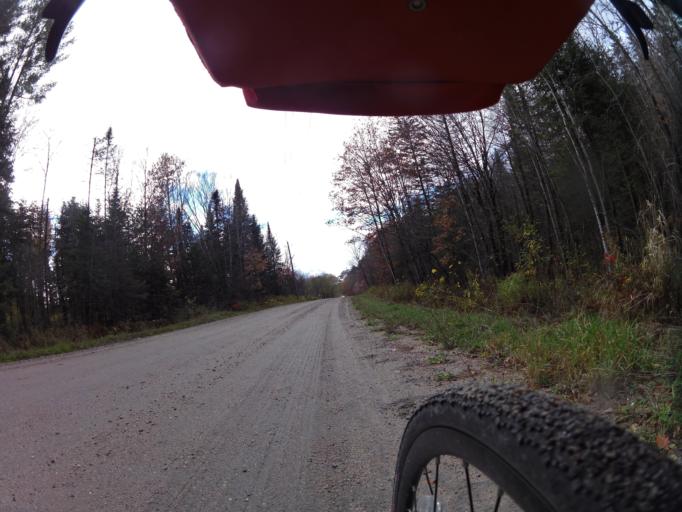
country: CA
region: Quebec
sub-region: Outaouais
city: Wakefield
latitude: 45.6973
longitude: -76.0453
